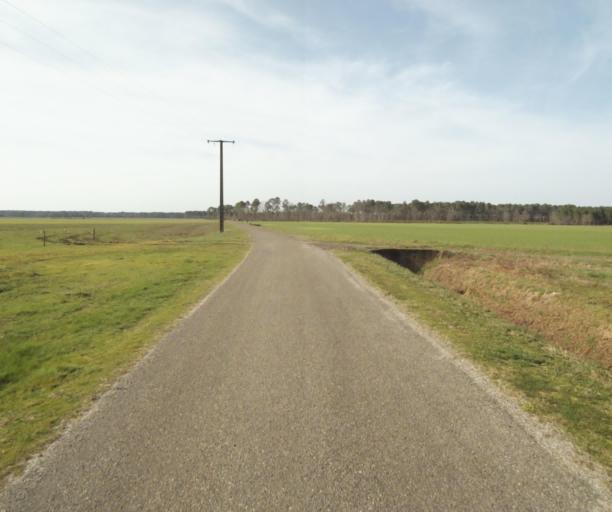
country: FR
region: Aquitaine
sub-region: Departement des Landes
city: Roquefort
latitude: 44.1528
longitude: -0.1658
